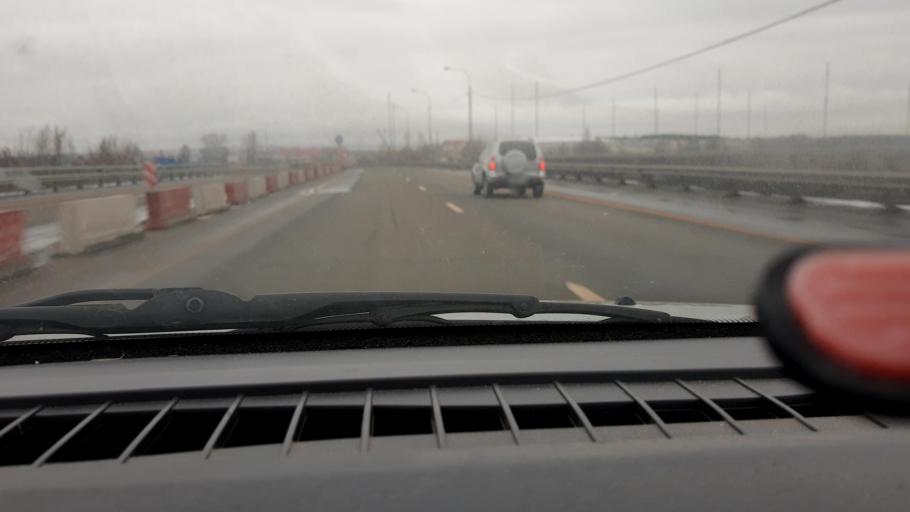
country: RU
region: Nizjnij Novgorod
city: Burevestnik
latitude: 56.1555
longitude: 43.9106
